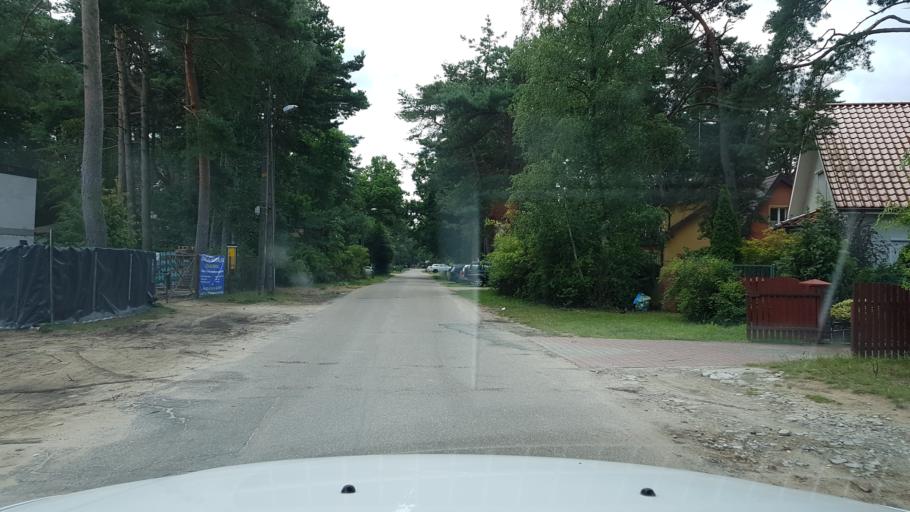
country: PL
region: West Pomeranian Voivodeship
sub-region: Powiat gryficki
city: Pobierowo
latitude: 54.0595
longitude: 14.9419
